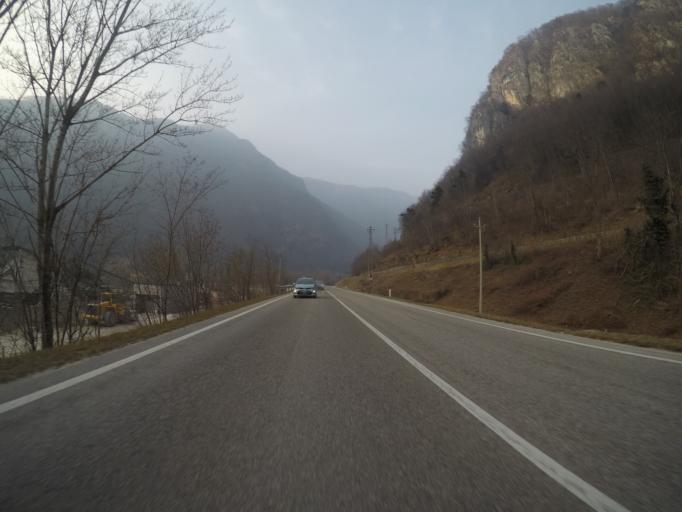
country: IT
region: Veneto
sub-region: Provincia di Belluno
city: Vas
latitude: 45.9400
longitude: 11.9252
